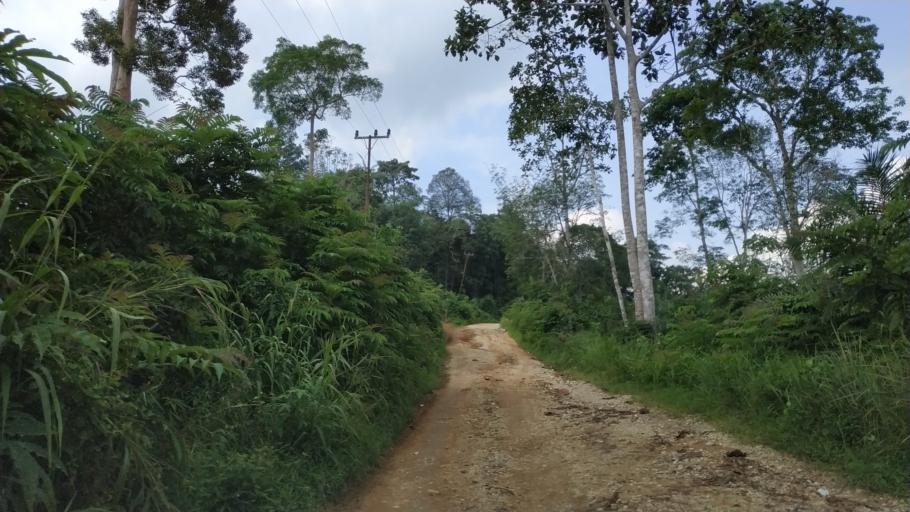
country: ID
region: Riau
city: Pangkalan Kasai
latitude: -0.7264
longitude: 102.4768
